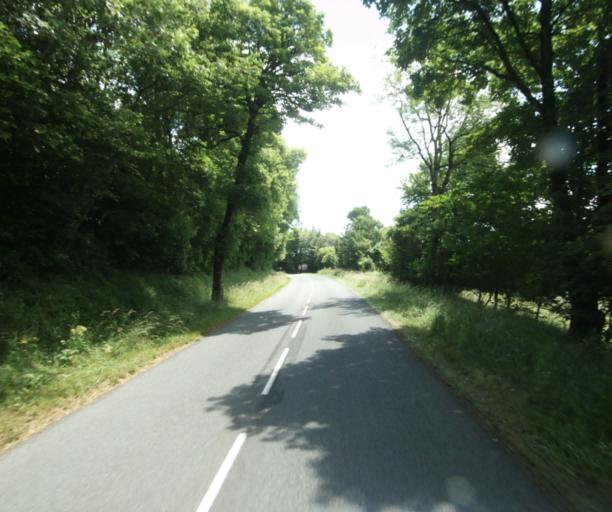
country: FR
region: Midi-Pyrenees
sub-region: Departement du Tarn
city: Soreze
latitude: 43.4123
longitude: 2.0735
